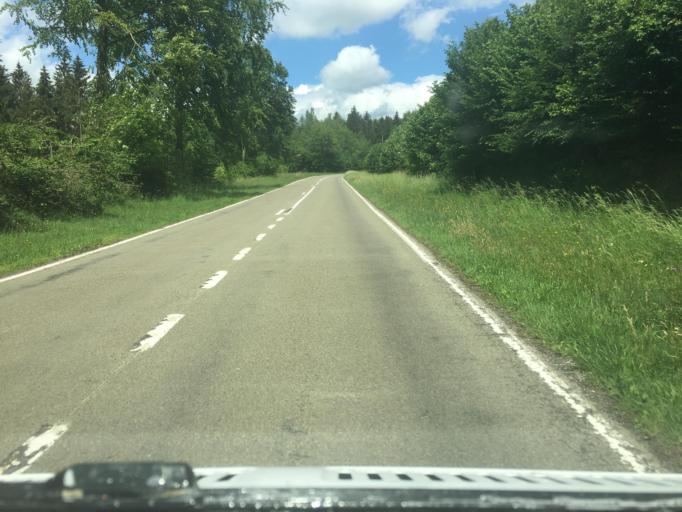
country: BE
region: Wallonia
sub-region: Province du Luxembourg
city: Florenville
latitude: 49.6635
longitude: 5.3310
